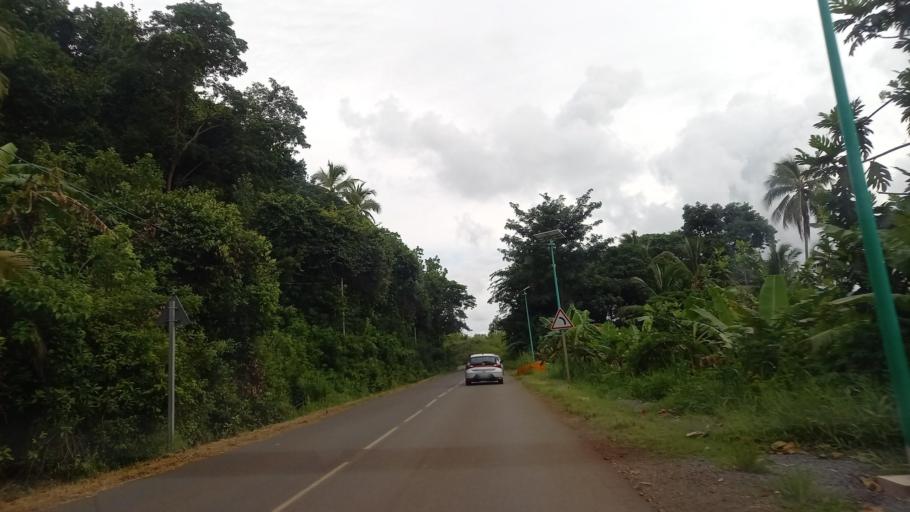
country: YT
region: Chirongui
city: Chirongui
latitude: -12.8979
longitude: 45.1444
